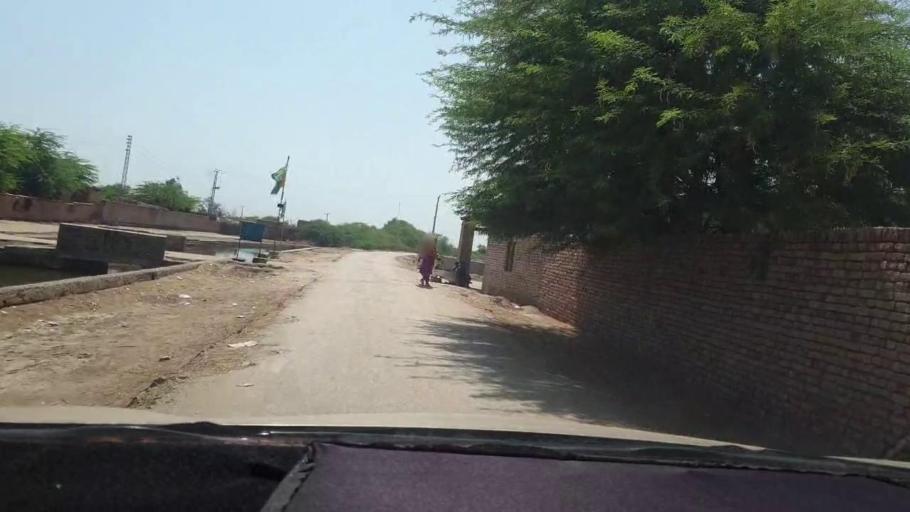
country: PK
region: Sindh
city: Shahdadkot
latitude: 27.8355
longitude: 67.9387
